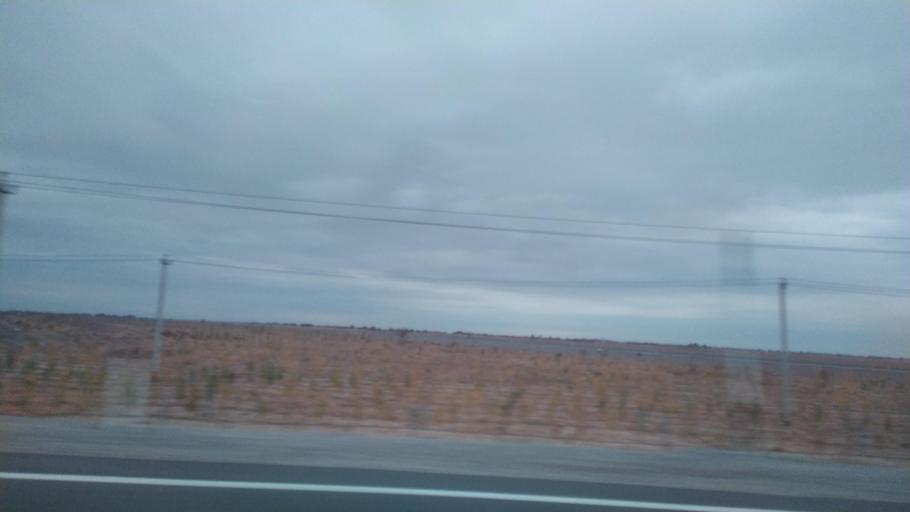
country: KZ
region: Ongtustik Qazaqstan
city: Turkestan
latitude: 43.2768
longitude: 68.4217
